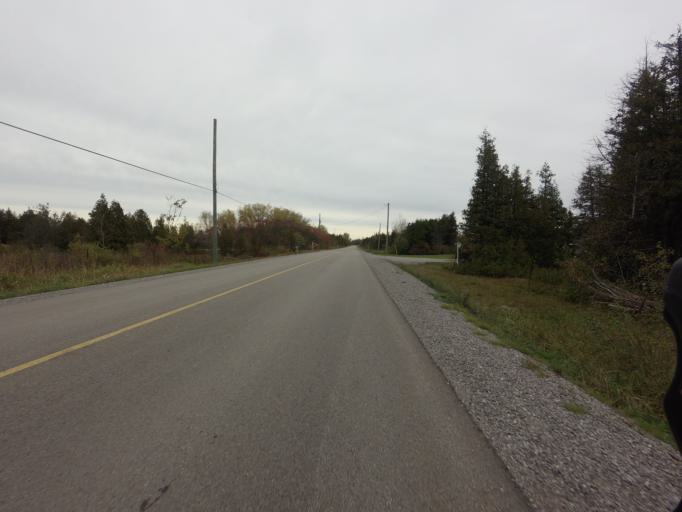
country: CA
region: Ontario
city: Brockville
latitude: 44.7749
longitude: -75.7574
